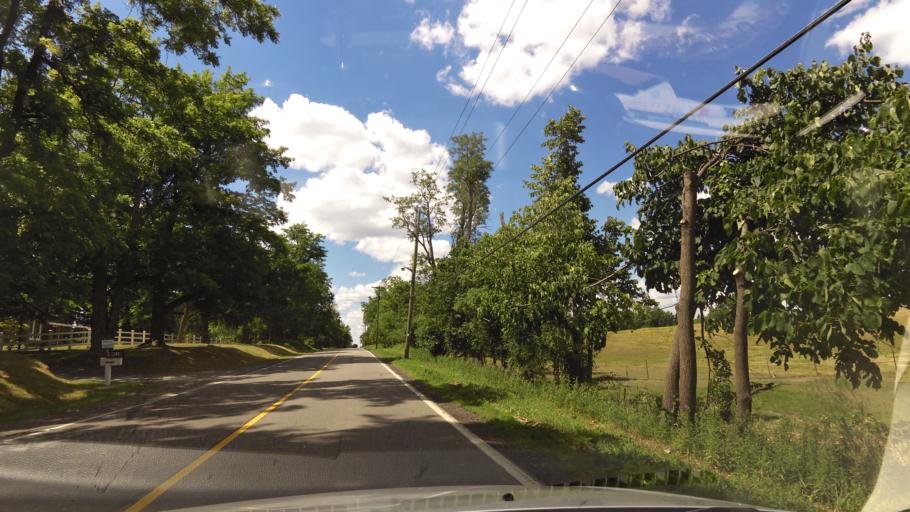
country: CA
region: Ontario
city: Brampton
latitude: 43.6294
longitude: -79.8275
